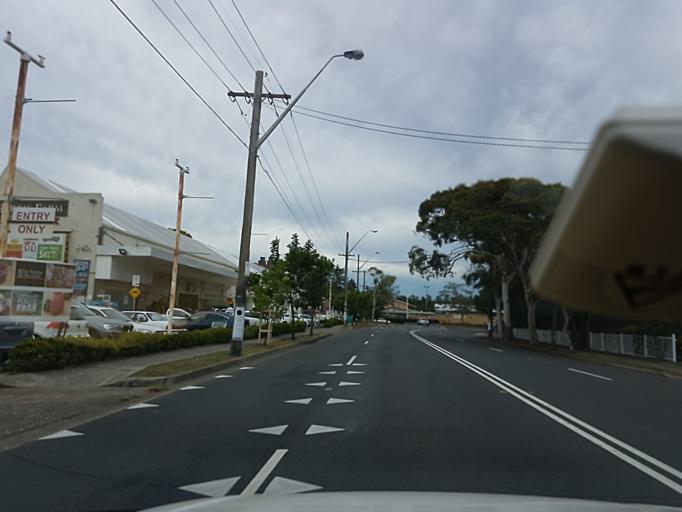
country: AU
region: New South Wales
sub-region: Warringah
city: Freshwater
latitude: -33.7869
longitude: 151.2823
